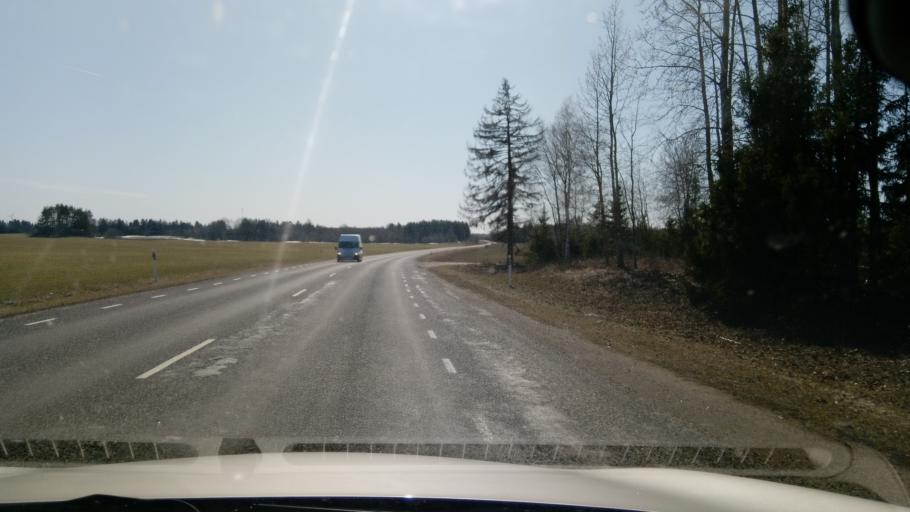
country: EE
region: Laeaene-Virumaa
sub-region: Rakvere linn
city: Rakvere
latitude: 59.2498
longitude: 26.2793
